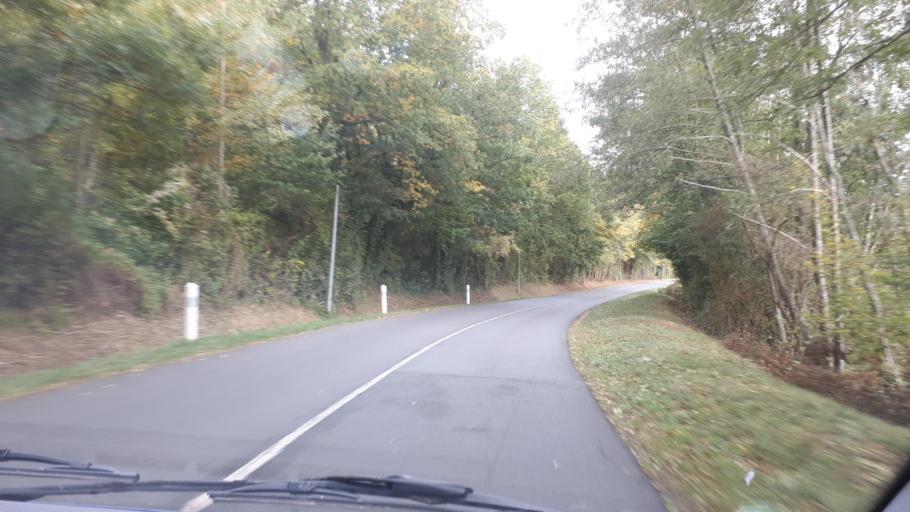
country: FR
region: Centre
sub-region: Departement du Loir-et-Cher
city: Mondoubleau
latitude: 47.9893
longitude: 0.8968
